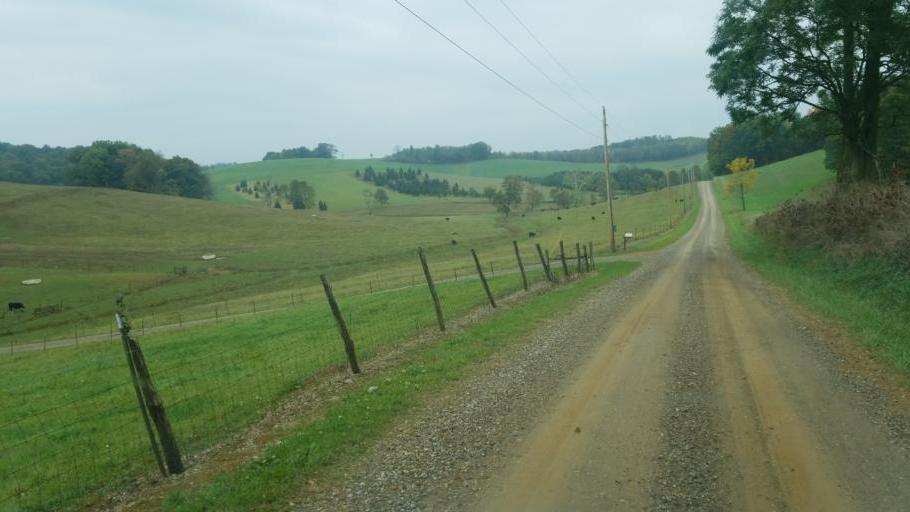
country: US
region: Ohio
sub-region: Knox County
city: Danville
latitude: 40.5085
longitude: -82.3427
